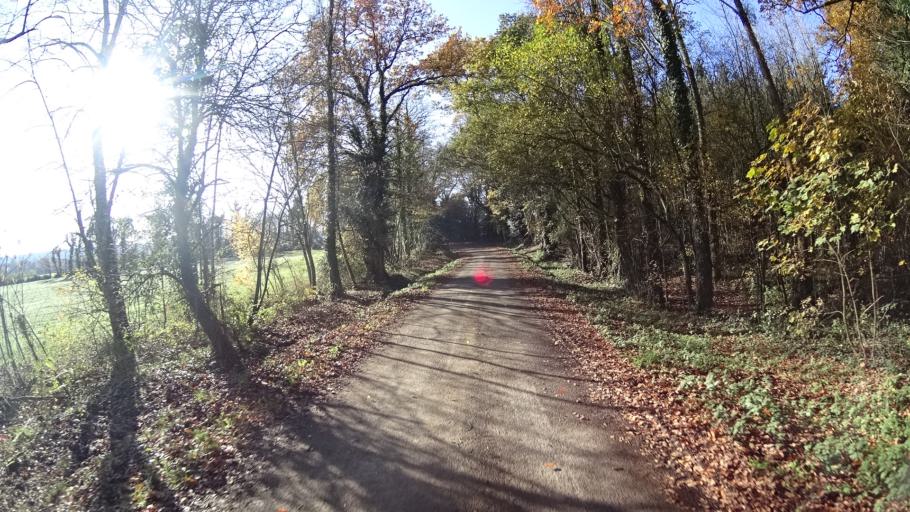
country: FR
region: Brittany
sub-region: Departement du Morbihan
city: Carentoir
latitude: 47.7910
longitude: -2.1980
